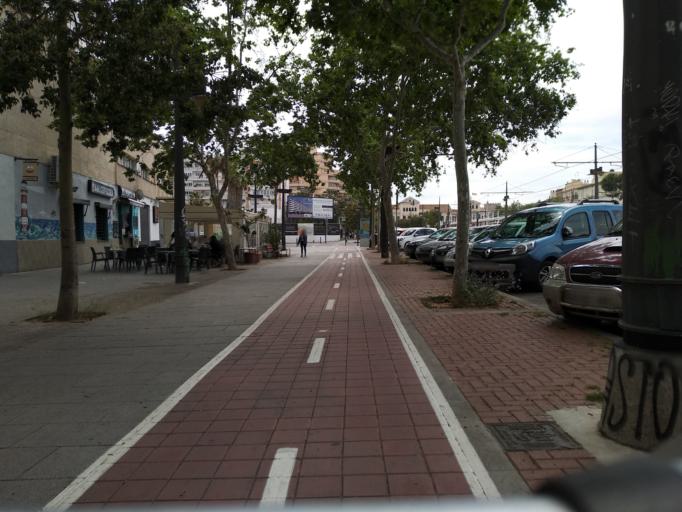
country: ES
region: Valencia
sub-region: Provincia de Valencia
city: Valencia
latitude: 39.4830
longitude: -0.3720
